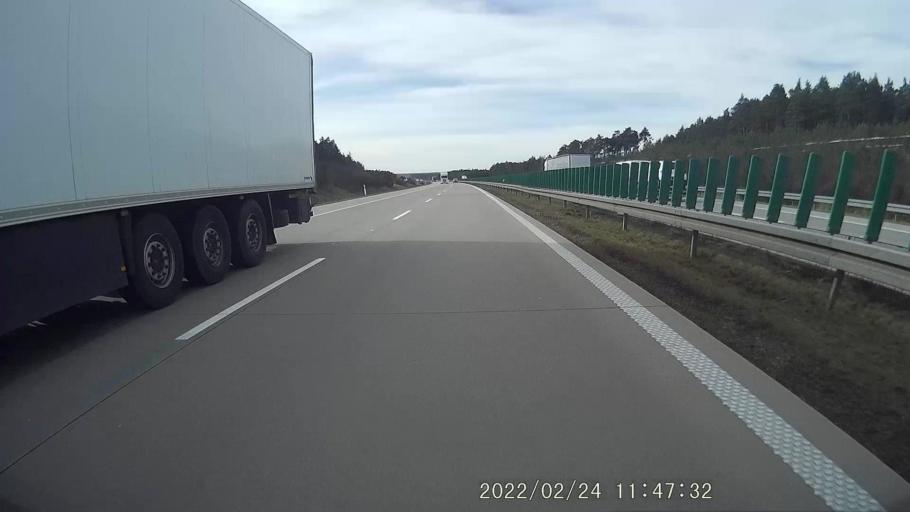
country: PL
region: Lower Silesian Voivodeship
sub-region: Powiat polkowicki
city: Radwanice
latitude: 51.5765
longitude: 15.9513
